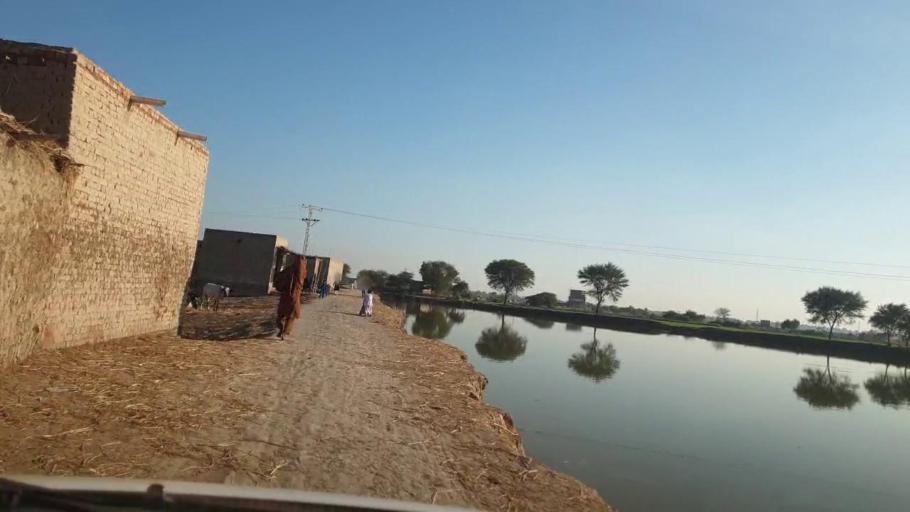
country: PK
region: Sindh
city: Khairpur Nathan Shah
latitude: 27.0461
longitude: 67.7253
